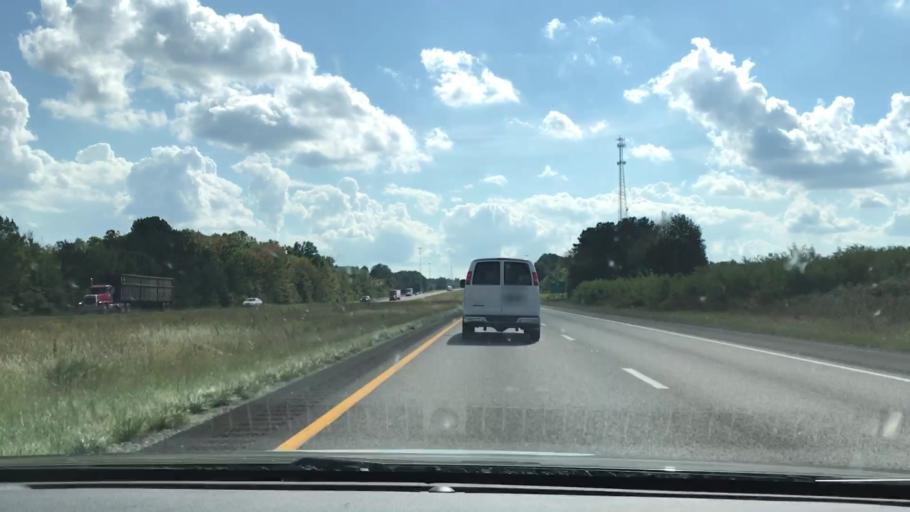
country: US
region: Tennessee
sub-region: Sumner County
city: White House
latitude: 36.4769
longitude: -86.6789
